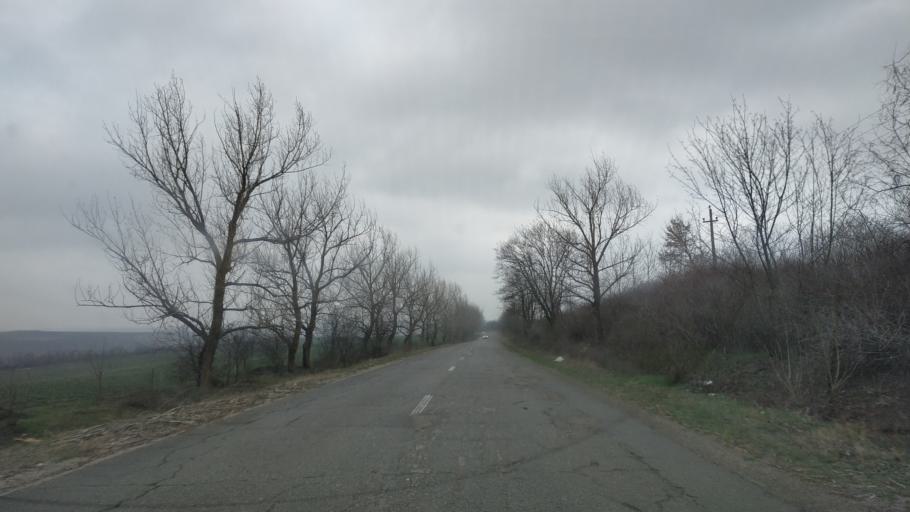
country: MD
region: Gagauzia
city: Bugeac
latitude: 46.3498
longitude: 28.7847
